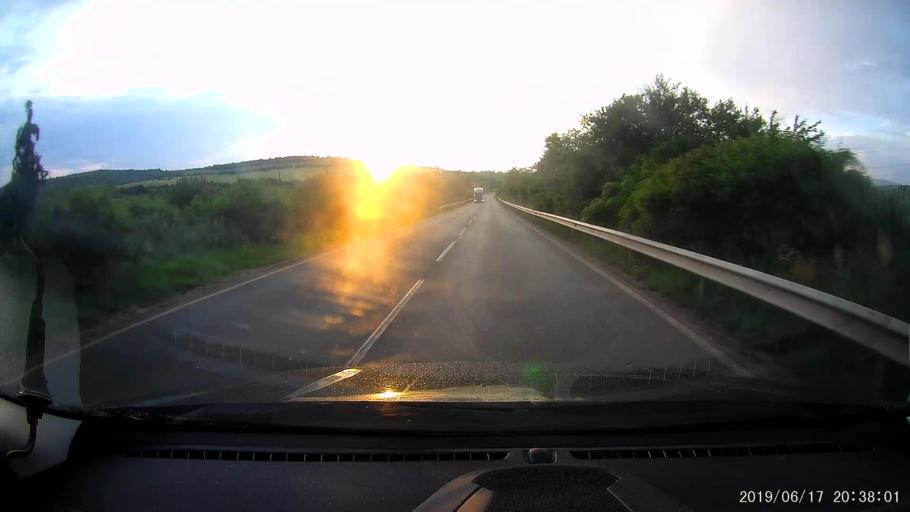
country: BG
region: Sofiya
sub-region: Obshtina Slivnitsa
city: Slivnitsa
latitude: 42.8676
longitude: 23.0234
